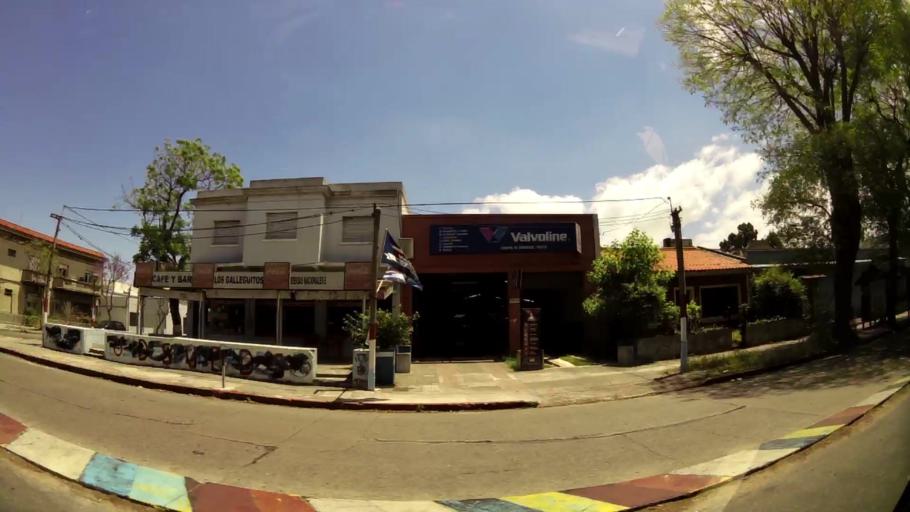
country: UY
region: Montevideo
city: Montevideo
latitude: -34.8707
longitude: -56.1966
